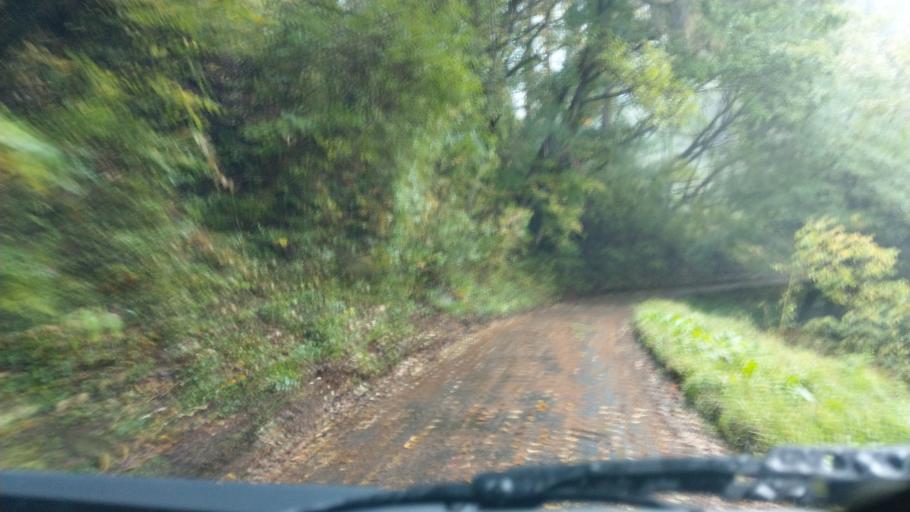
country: JP
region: Nagano
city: Komoro
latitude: 36.3691
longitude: 138.4494
